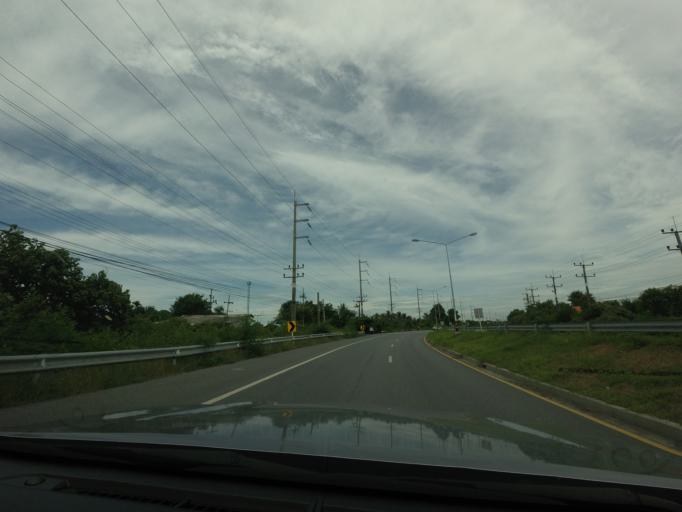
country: TH
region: Songkhla
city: Ranot
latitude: 7.8047
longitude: 100.3604
